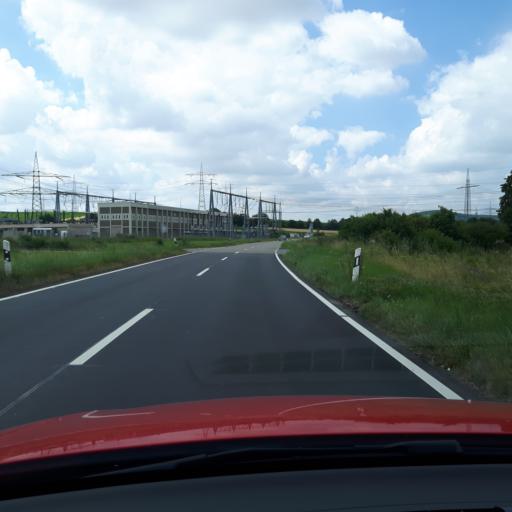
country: DE
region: Baden-Wuerttemberg
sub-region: Regierungsbezirk Stuttgart
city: Leingarten
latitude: 49.1445
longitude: 9.1505
